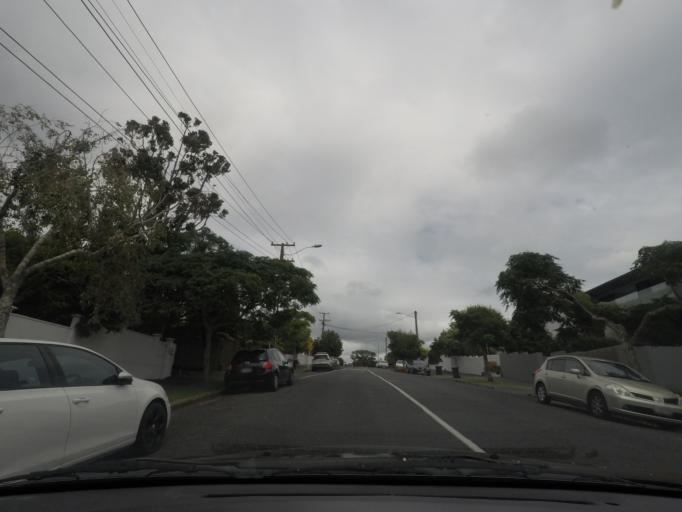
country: NZ
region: Auckland
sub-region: Auckland
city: Auckland
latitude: -36.8702
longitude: 174.7843
